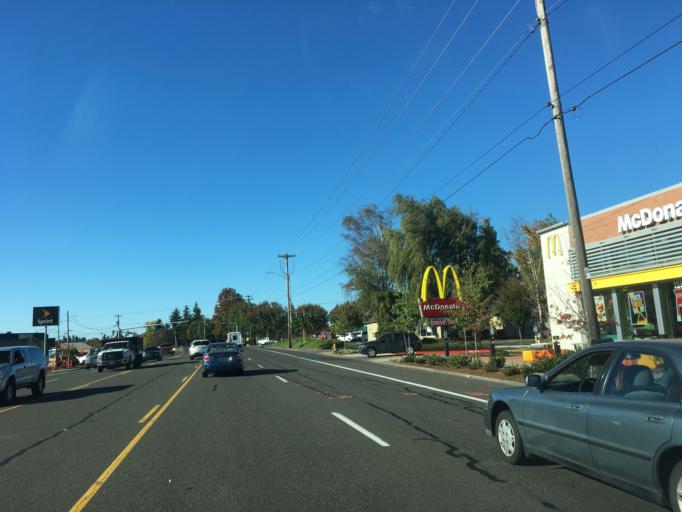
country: US
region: Oregon
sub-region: Multnomah County
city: Gresham
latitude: 45.5037
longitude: -122.4160
